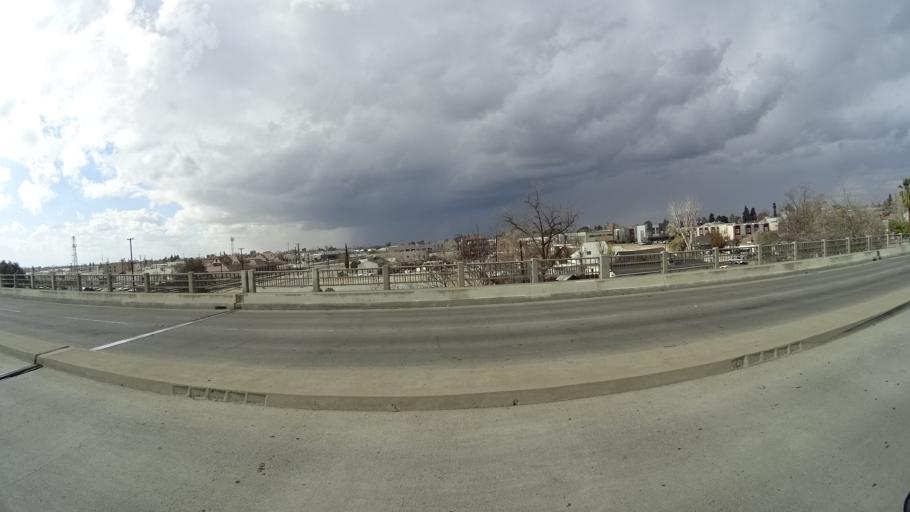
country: US
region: California
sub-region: Kern County
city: Bakersfield
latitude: 35.3775
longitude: -118.9889
